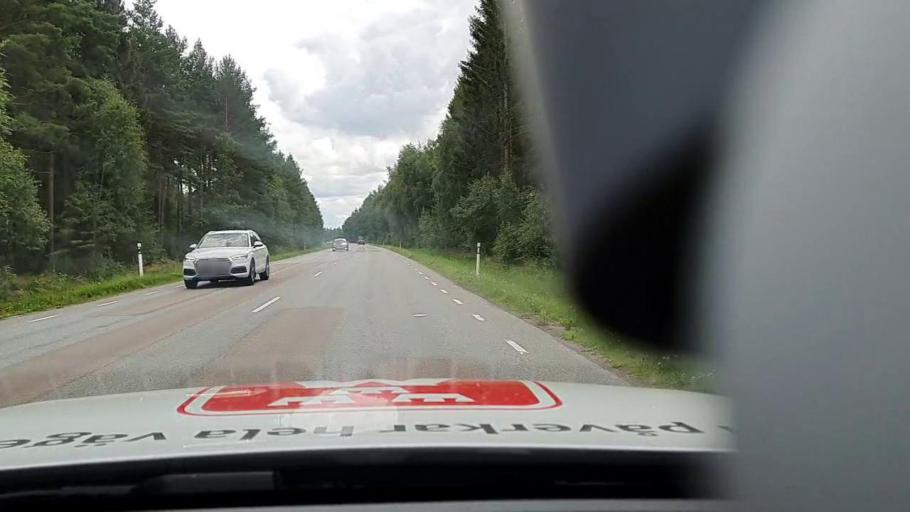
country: SE
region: Vaestra Goetaland
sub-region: Lidkopings Kommun
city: Lidkoping
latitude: 58.5162
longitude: 13.1148
